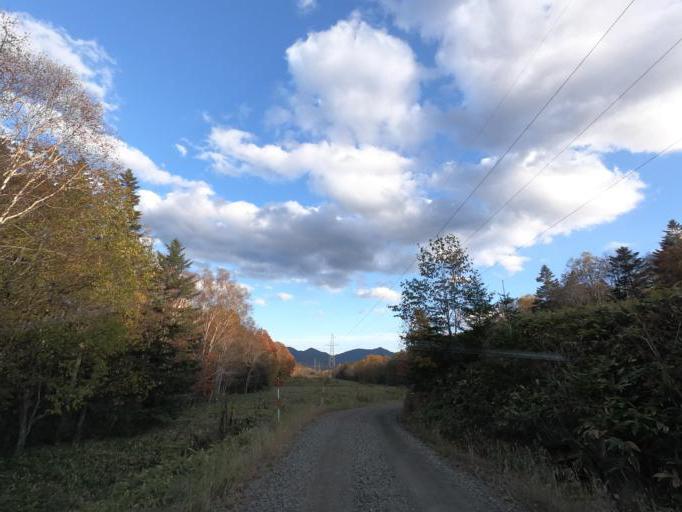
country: JP
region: Hokkaido
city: Otofuke
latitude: 43.4329
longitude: 143.1594
